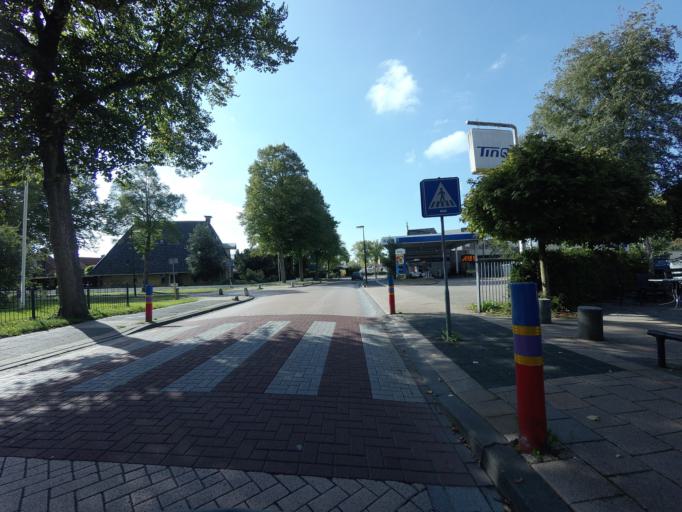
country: NL
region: Friesland
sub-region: Sudwest Fryslan
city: Bolsward
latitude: 53.0611
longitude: 5.5303
